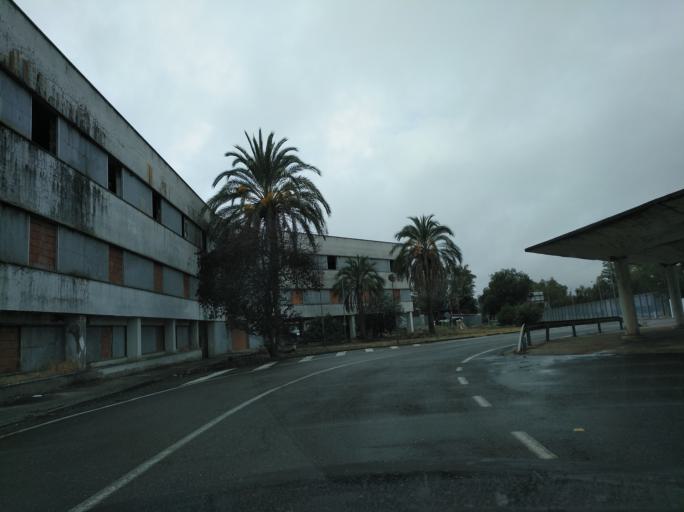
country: ES
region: Extremadura
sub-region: Provincia de Badajoz
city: Badajoz
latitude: 38.8830
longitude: -7.0325
